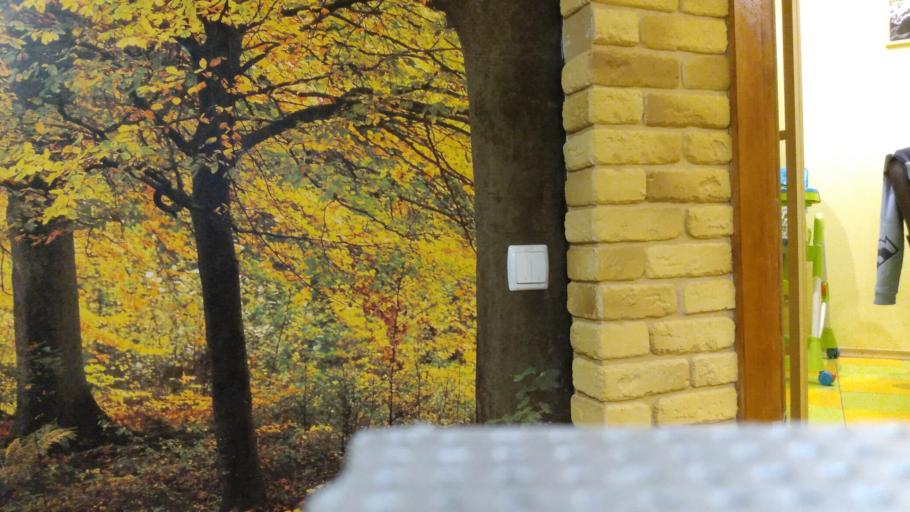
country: RU
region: Vologda
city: Babayevo
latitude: 59.3625
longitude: 36.0012
